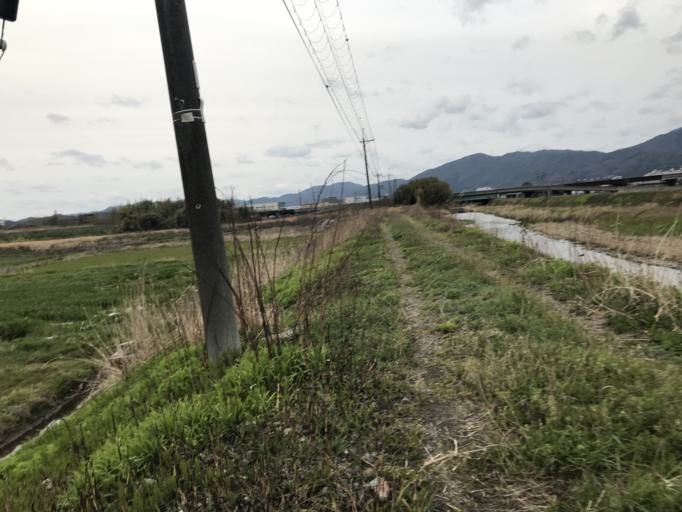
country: JP
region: Kyoto
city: Kameoka
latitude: 35.0194
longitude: 135.5491
